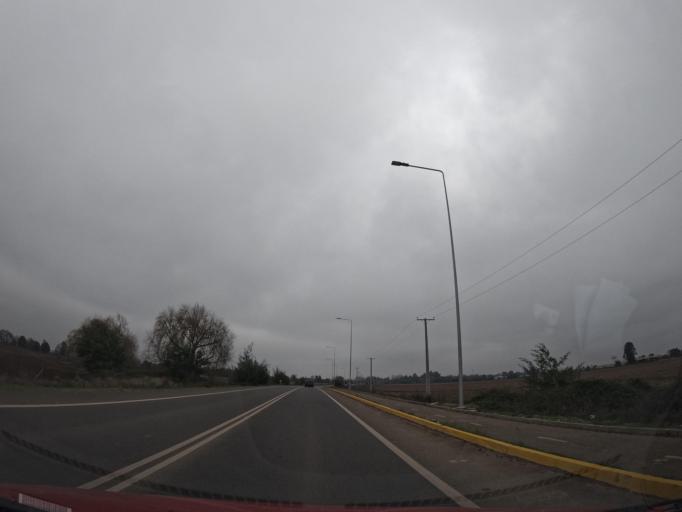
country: CL
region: Maule
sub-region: Provincia de Talca
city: San Clemente
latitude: -35.5367
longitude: -71.4732
